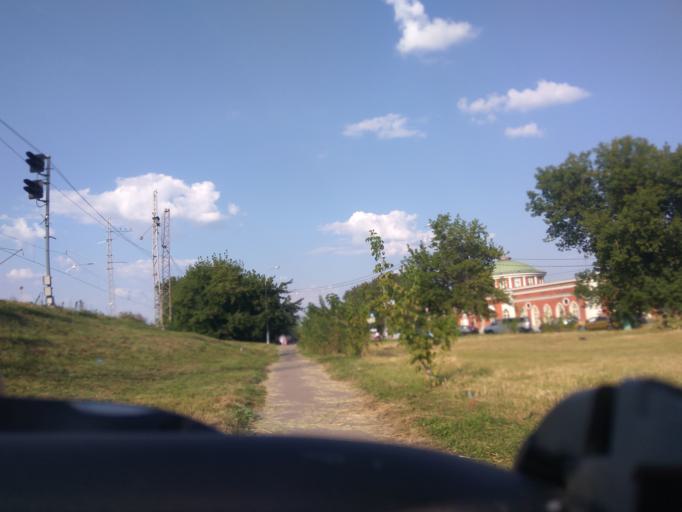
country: RU
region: Moscow
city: Orekhovo-Borisovo Severnoye
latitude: 55.6185
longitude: 37.6714
